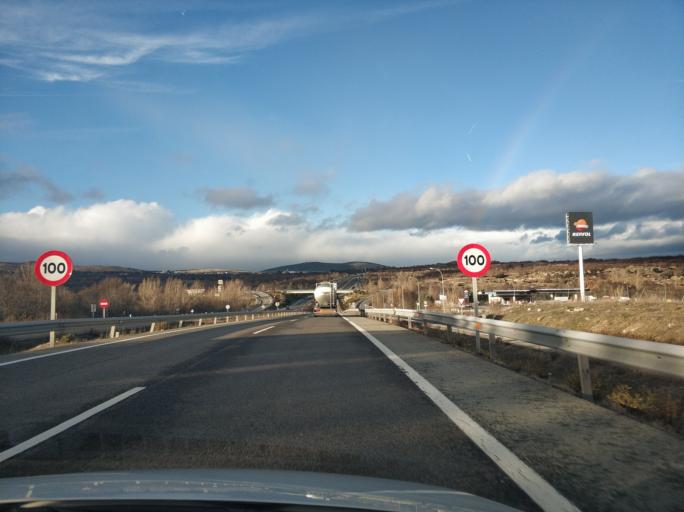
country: ES
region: Madrid
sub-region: Provincia de Madrid
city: La Cabrera
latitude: 40.9032
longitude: -3.6083
